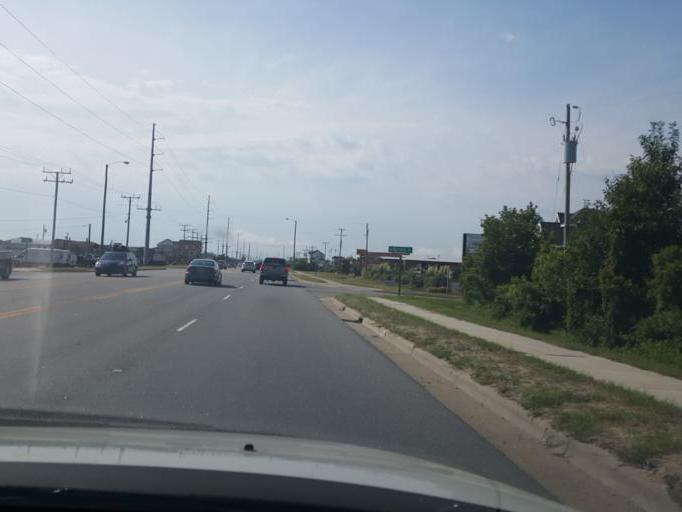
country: US
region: North Carolina
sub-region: Dare County
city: Kill Devil Hills
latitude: 36.0451
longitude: -75.6800
